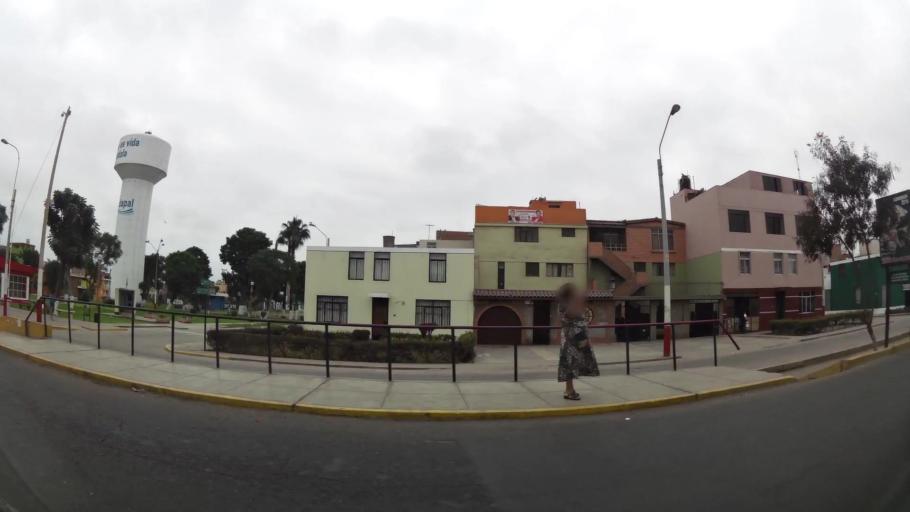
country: PE
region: Callao
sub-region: Callao
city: Callao
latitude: -12.0555
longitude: -77.1086
